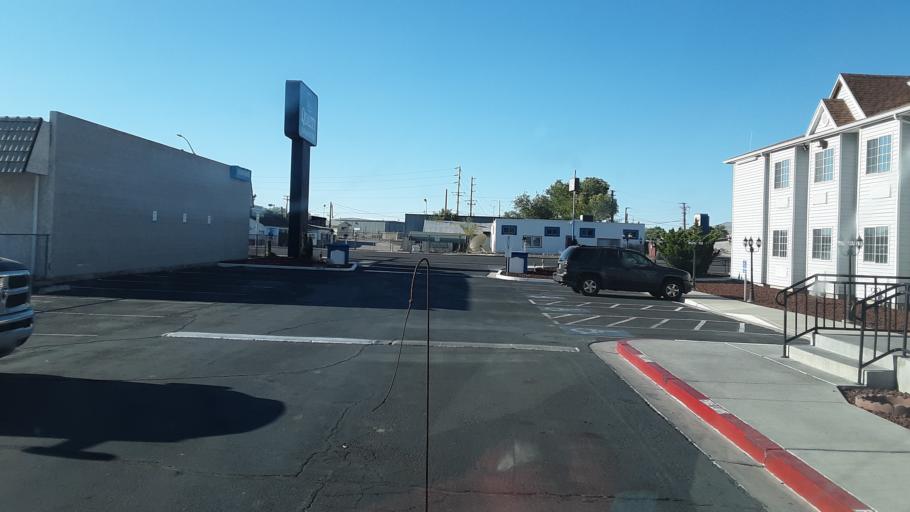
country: US
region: Nevada
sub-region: Churchill County
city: Fallon
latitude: 39.4737
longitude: -118.7904
